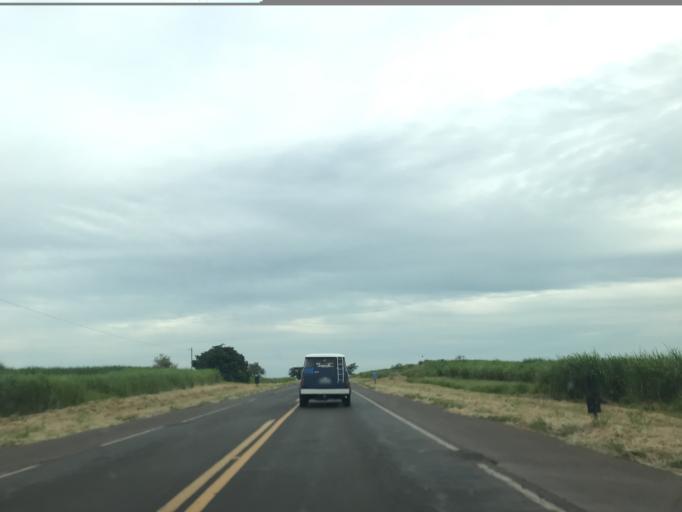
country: BR
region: Sao Paulo
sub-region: Tupa
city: Tupa
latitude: -21.6272
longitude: -50.4875
